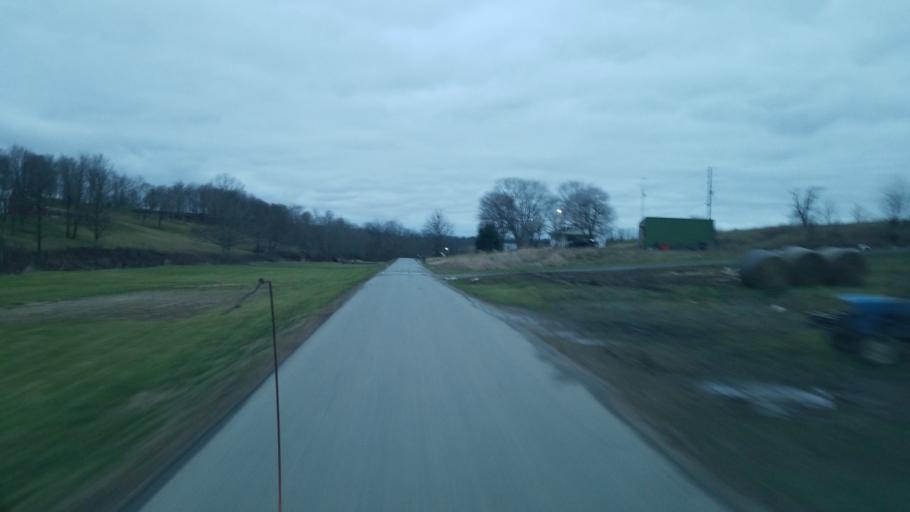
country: US
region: Kentucky
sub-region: Fleming County
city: Flemingsburg
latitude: 38.5050
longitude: -83.6899
